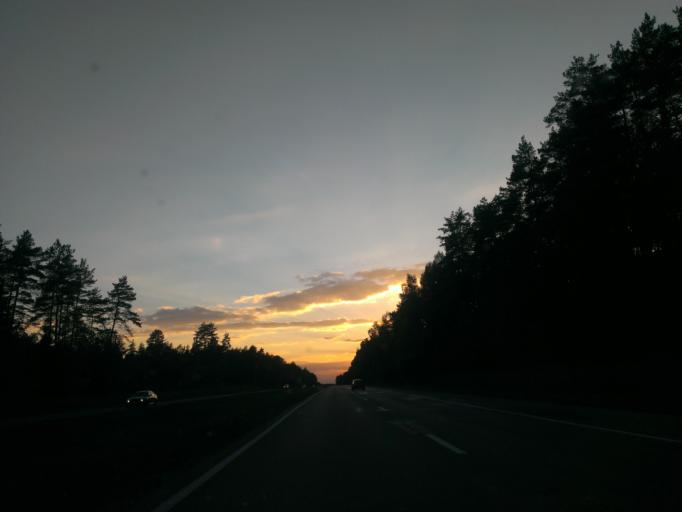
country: LV
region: Incukalns
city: Incukalns
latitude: 57.1224
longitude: 24.6726
